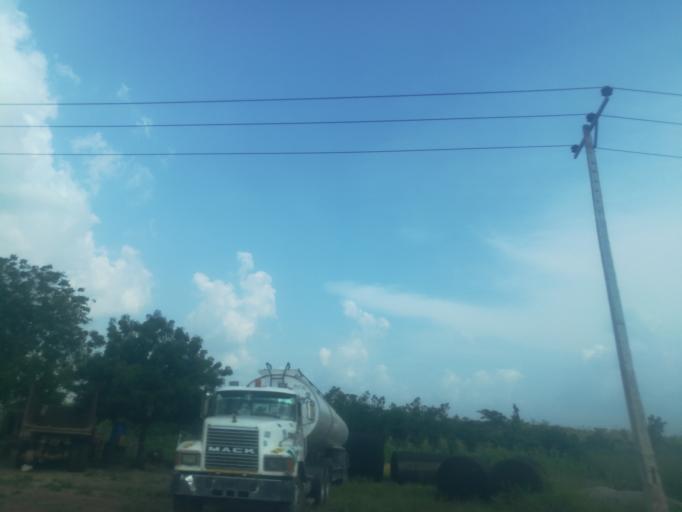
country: NG
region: Ogun
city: Abeokuta
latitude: 7.1055
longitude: 3.2973
